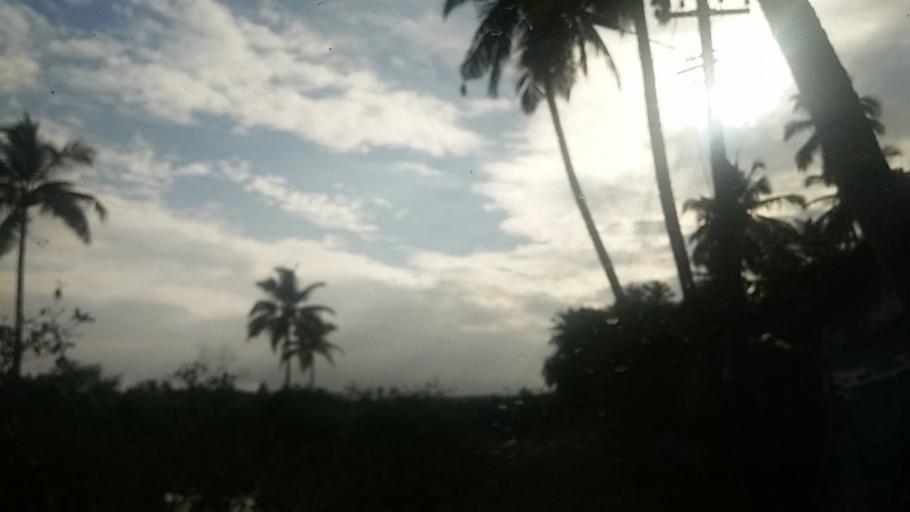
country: IN
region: Goa
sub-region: South Goa
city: Cavelossim
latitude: 15.1757
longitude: 73.9633
